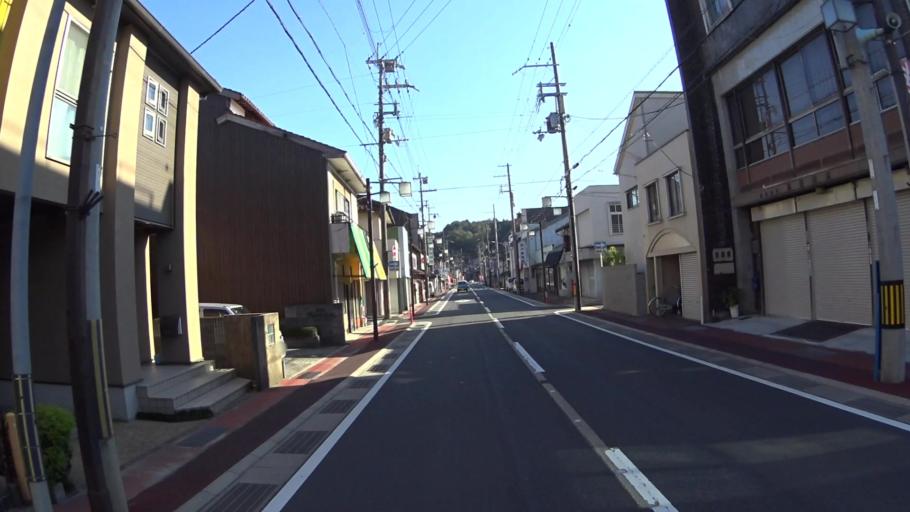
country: JP
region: Kyoto
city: Miyazu
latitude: 35.6237
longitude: 135.0588
